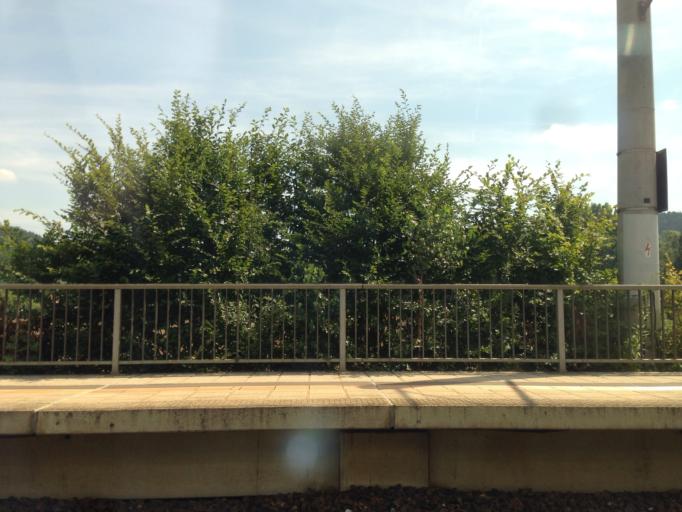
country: DE
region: Thuringia
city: Rothenstein
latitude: 50.8512
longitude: 11.6093
